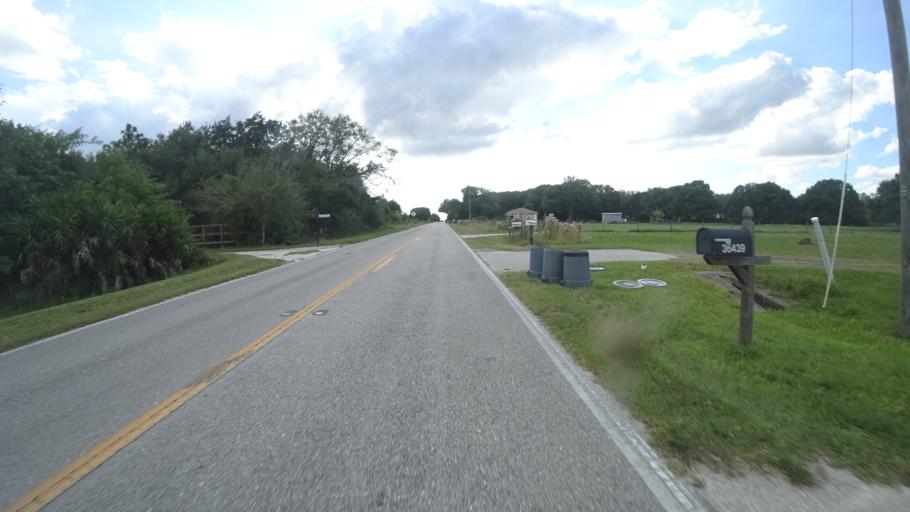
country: US
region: Florida
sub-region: Sarasota County
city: Lake Sarasota
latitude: 27.3442
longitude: -82.1691
